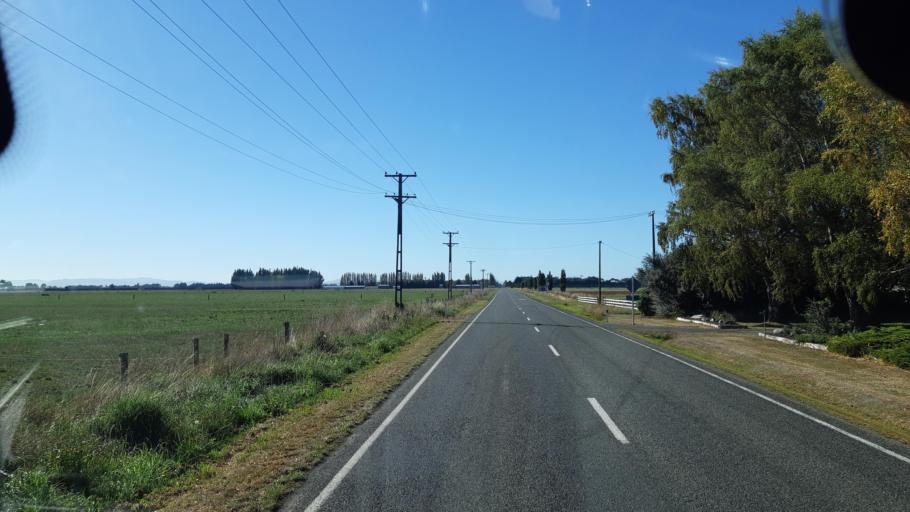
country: NZ
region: Southland
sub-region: Southland District
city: Winton
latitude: -46.1490
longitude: 168.1525
